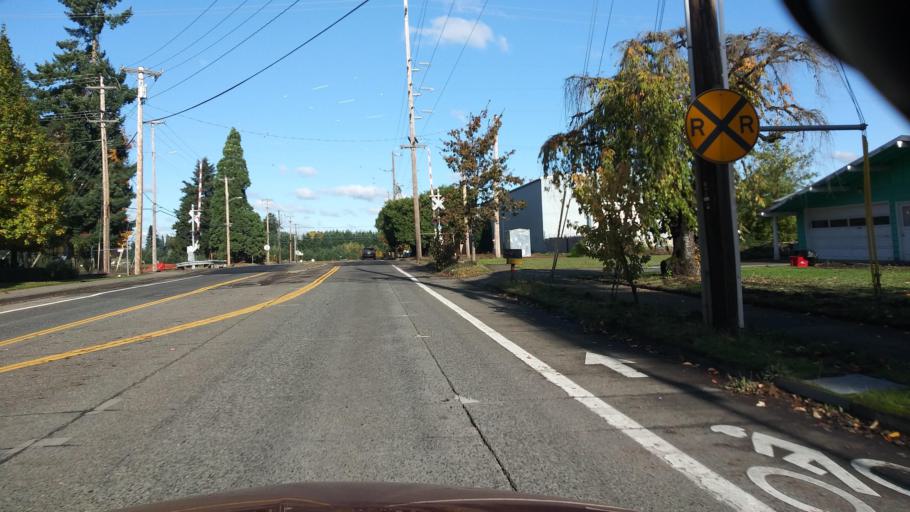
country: US
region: Oregon
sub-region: Washington County
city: Cornelius
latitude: 45.5234
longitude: -123.0841
